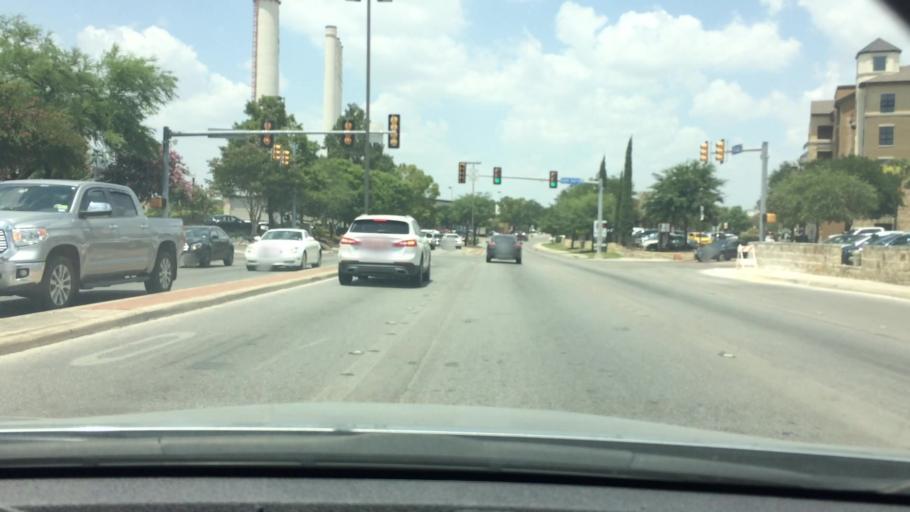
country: US
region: Texas
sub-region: Bexar County
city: Alamo Heights
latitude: 29.4938
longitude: -98.4795
